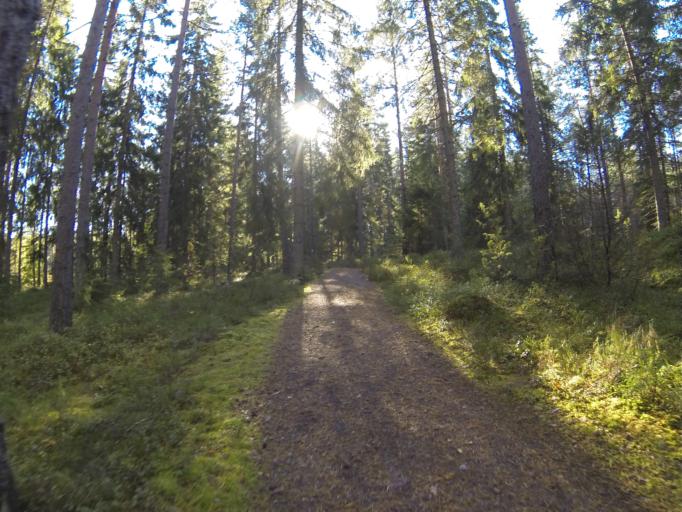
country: FI
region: Varsinais-Suomi
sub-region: Salo
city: Saerkisalo
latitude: 60.2082
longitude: 22.9401
